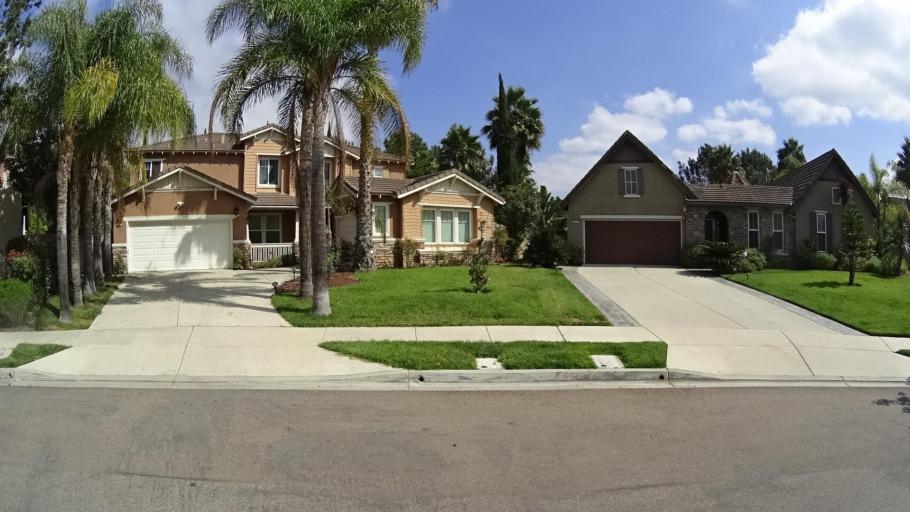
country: US
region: California
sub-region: San Diego County
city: Poway
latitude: 33.0030
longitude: -117.1017
